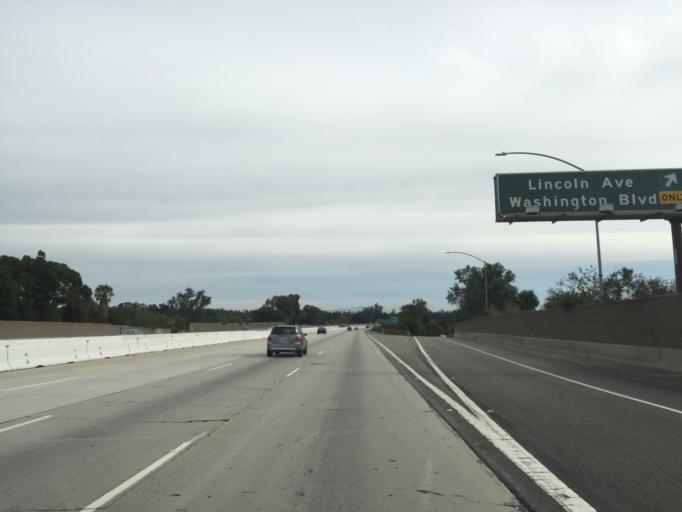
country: US
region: California
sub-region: Los Angeles County
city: La Canada Flintridge
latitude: 34.1769
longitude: -118.1634
